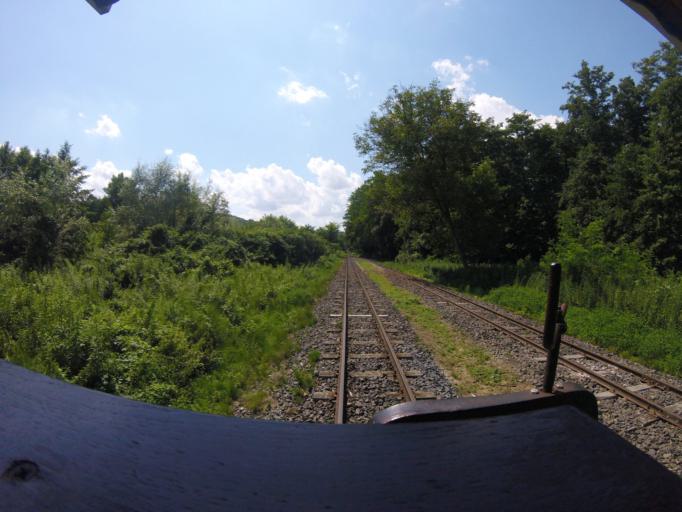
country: HU
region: Zala
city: Letenye
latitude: 46.5689
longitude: 16.6782
